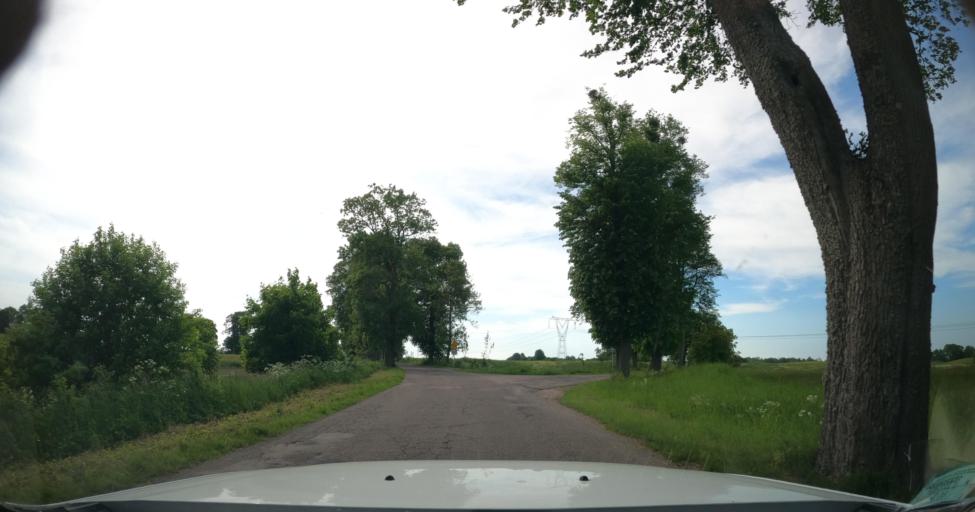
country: PL
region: Warmian-Masurian Voivodeship
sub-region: Powiat ostrodzki
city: Milakowo
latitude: 54.0177
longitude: 20.0504
